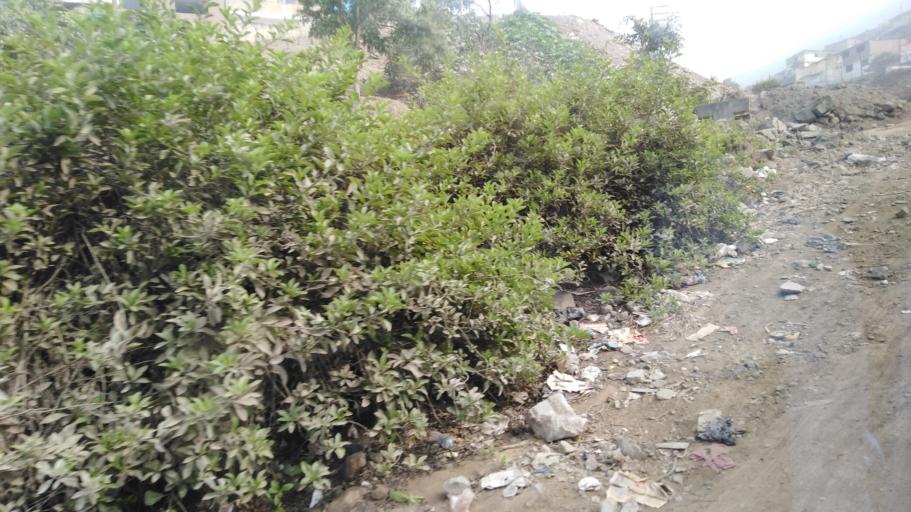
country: PE
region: Lima
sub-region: Lima
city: La Molina
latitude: -12.1450
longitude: -76.9252
